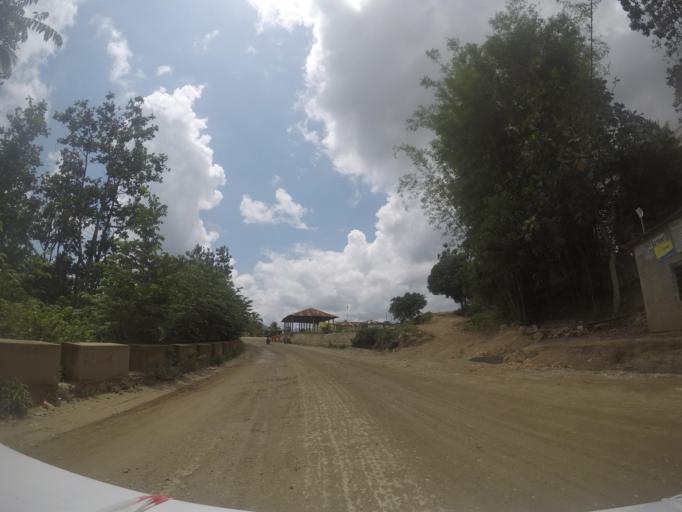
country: TL
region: Baucau
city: Venilale
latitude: -8.5908
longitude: 126.3870
